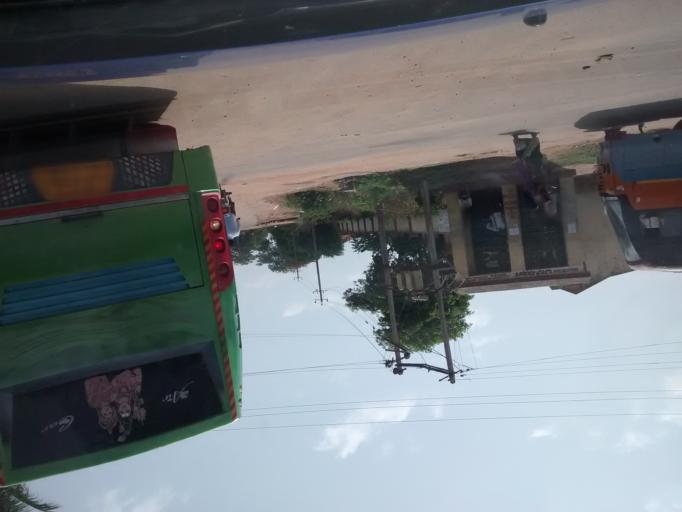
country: IN
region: Karnataka
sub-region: Hassan
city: Hole Narsipur
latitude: 12.6907
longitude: 76.1928
